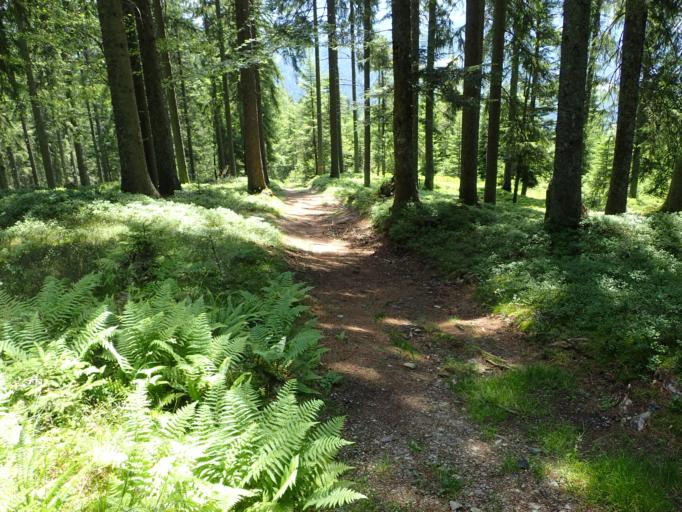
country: AT
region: Salzburg
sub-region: Politischer Bezirk Sankt Johann im Pongau
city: Filzmoos
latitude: 47.4553
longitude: 13.4631
